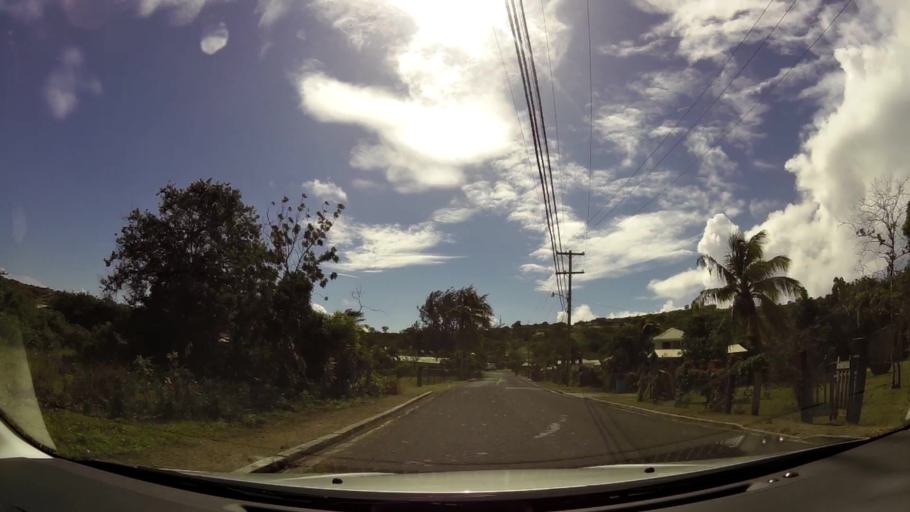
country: AG
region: Saint Paul
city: Falmouth
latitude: 17.0361
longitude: -61.7514
